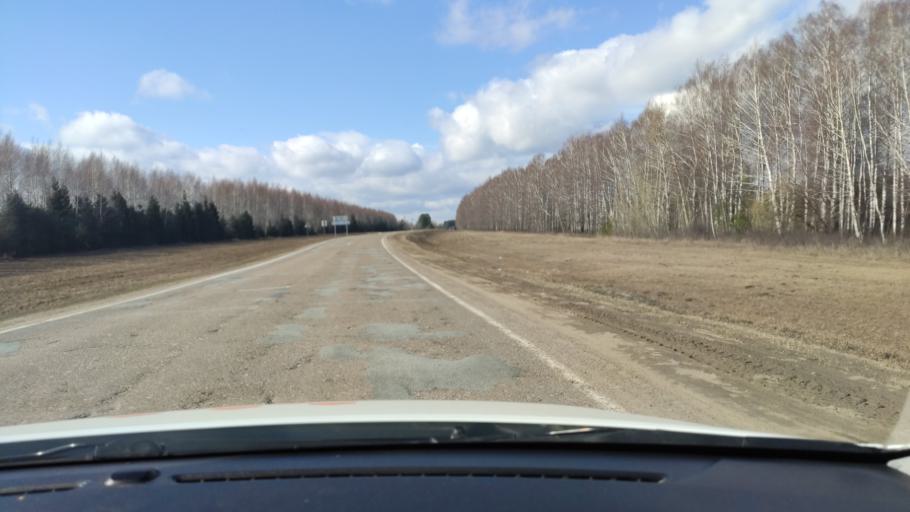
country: RU
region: Tatarstan
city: Vysokaya Gora
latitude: 56.0378
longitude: 49.2288
